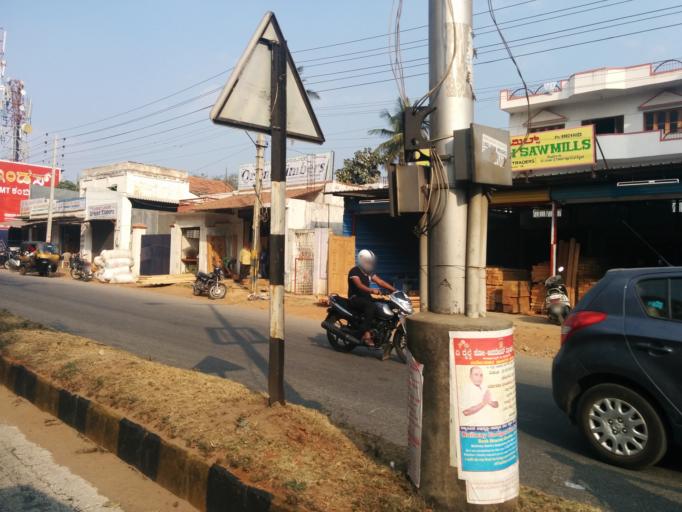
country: IN
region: Karnataka
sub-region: Mysore
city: Mysore
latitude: 12.2846
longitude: 76.6423
